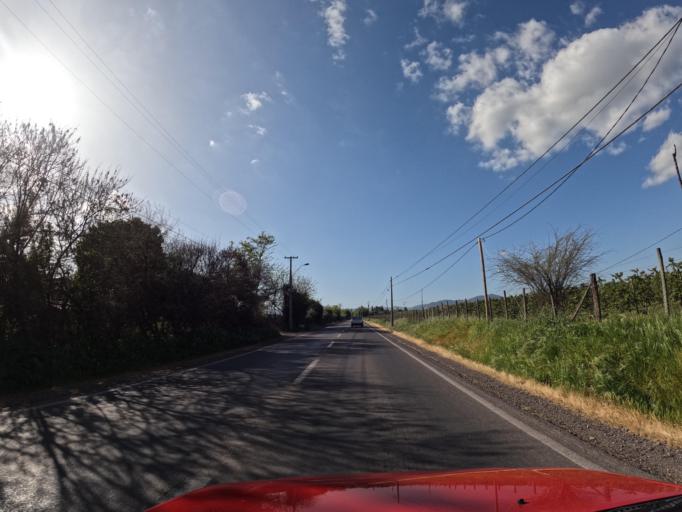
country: CL
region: Maule
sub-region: Provincia de Curico
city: Rauco
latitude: -34.9128
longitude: -71.2778
